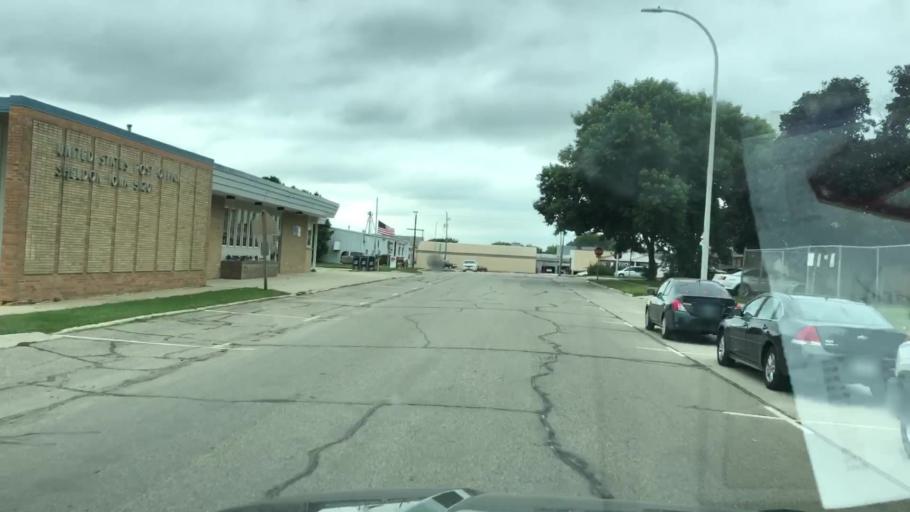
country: US
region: Iowa
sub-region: O'Brien County
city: Sheldon
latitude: 43.1784
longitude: -95.8547
